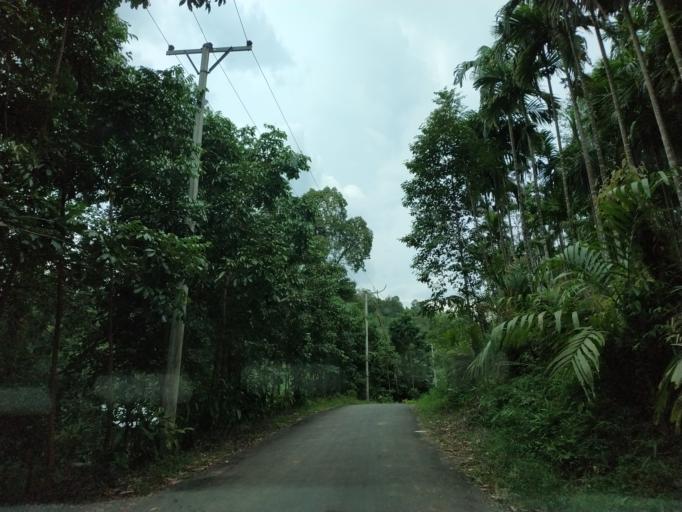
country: MM
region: Tanintharyi
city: Dawei
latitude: 13.8650
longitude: 98.2741
